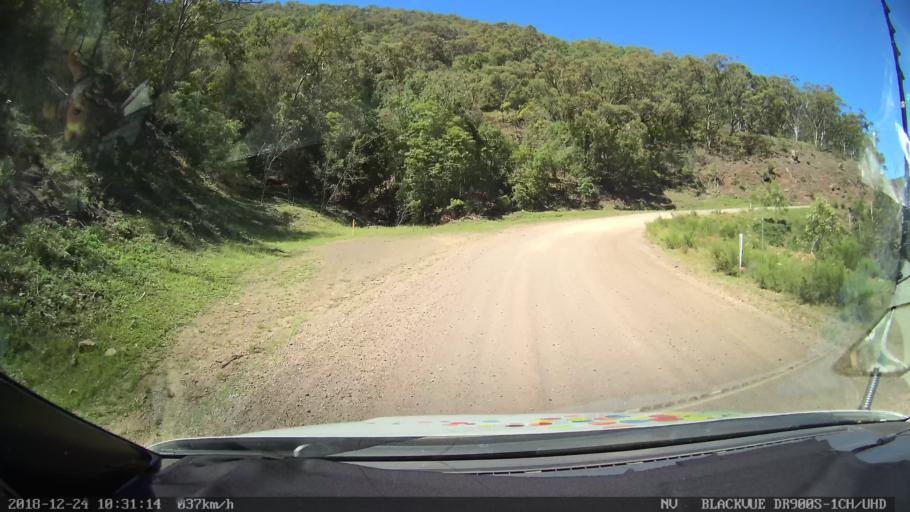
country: AU
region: New South Wales
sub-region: Upper Hunter Shire
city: Merriwa
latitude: -31.8388
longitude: 150.5228
